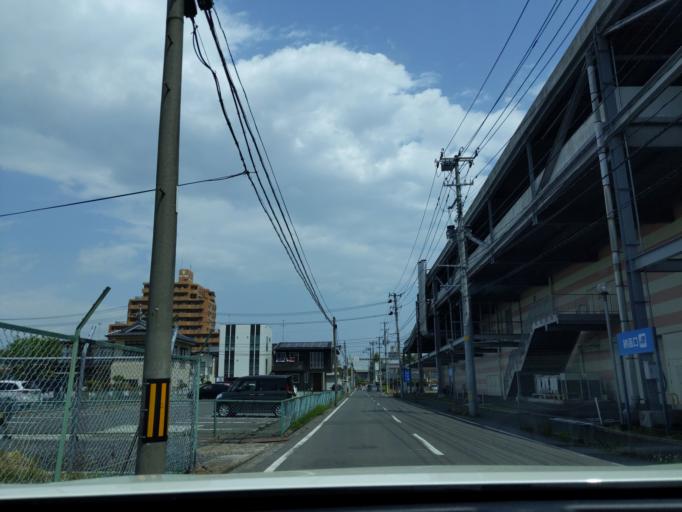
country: JP
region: Fukushima
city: Koriyama
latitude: 37.3974
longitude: 140.3694
